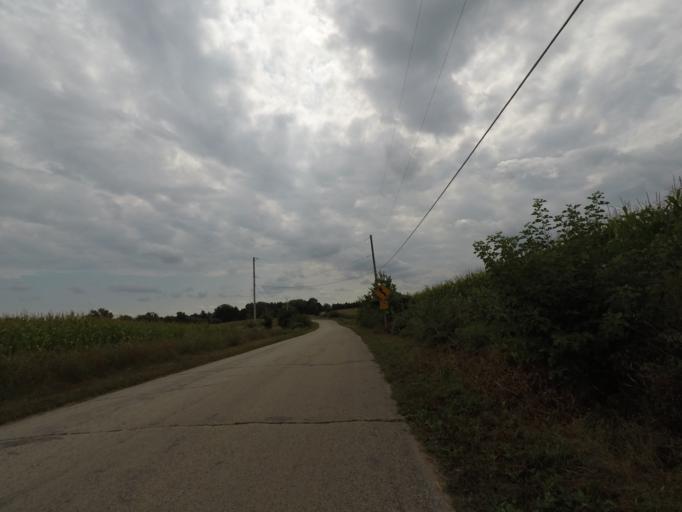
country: US
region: Wisconsin
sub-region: Jefferson County
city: Lake Koshkonong
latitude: 42.8950
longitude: -88.8736
